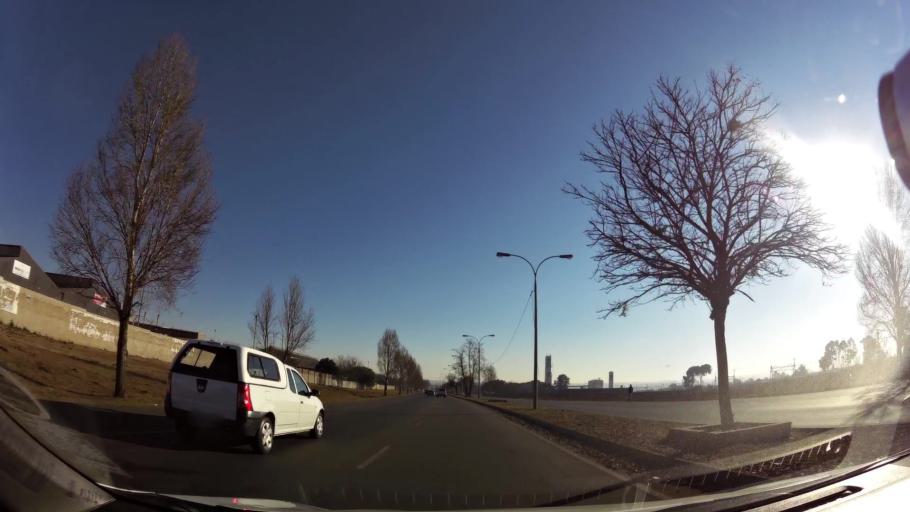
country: ZA
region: Gauteng
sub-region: Ekurhuleni Metropolitan Municipality
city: Germiston
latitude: -26.3171
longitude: 28.1398
